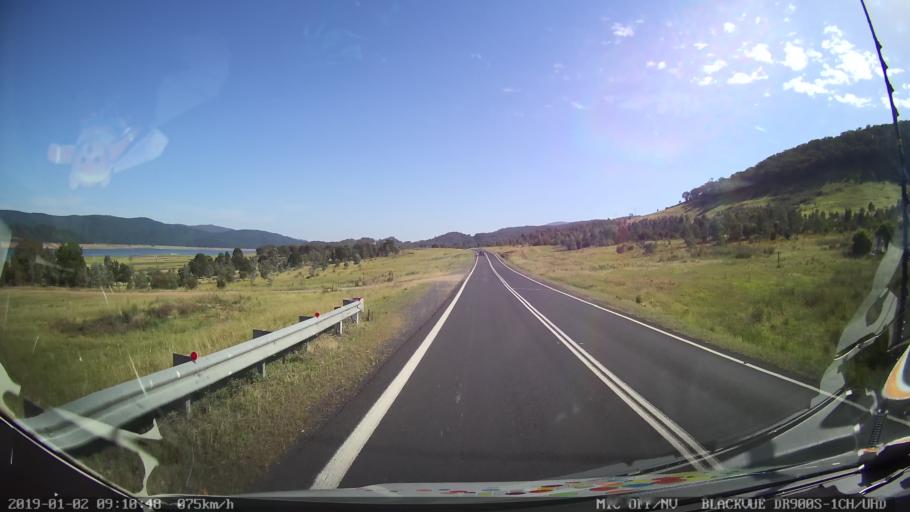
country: AU
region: New South Wales
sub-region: Tumut Shire
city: Tumut
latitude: -35.5182
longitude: 148.2684
